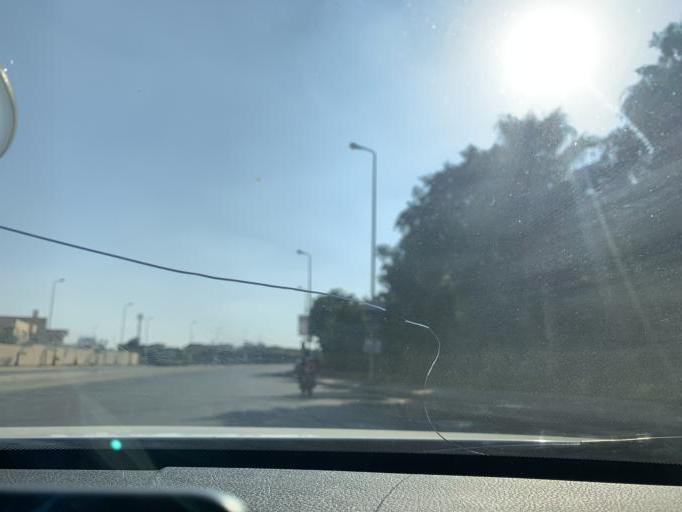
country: EG
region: Muhafazat al Qalyubiyah
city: Al Khankah
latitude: 30.0137
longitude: 31.4860
